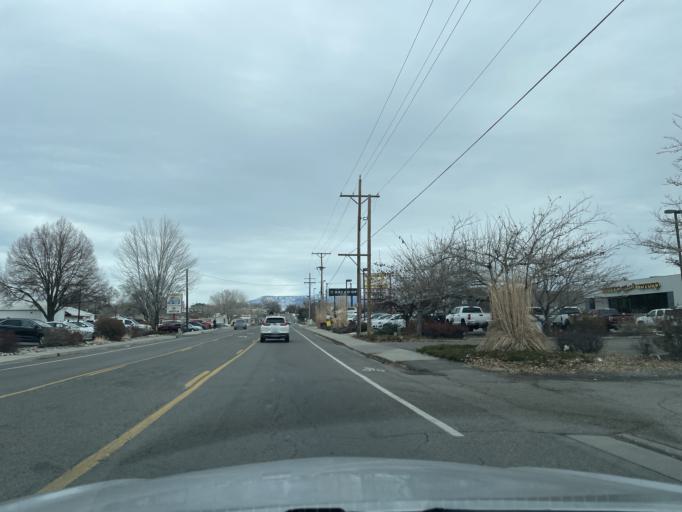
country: US
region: Colorado
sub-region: Mesa County
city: Grand Junction
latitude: 39.0810
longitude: -108.5822
